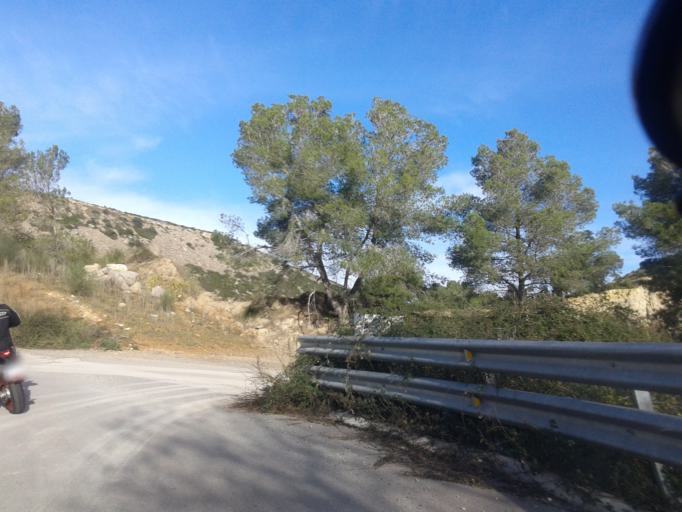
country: ES
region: Catalonia
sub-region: Provincia de Barcelona
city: Vilafranca del Penedes
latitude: 41.3091
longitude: 1.7233
